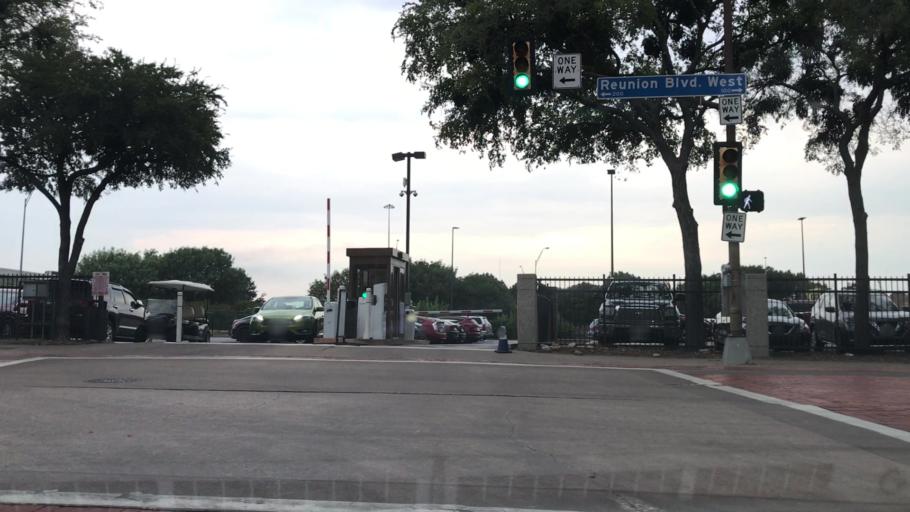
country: US
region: Texas
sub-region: Dallas County
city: Dallas
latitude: 32.7771
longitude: -96.8094
